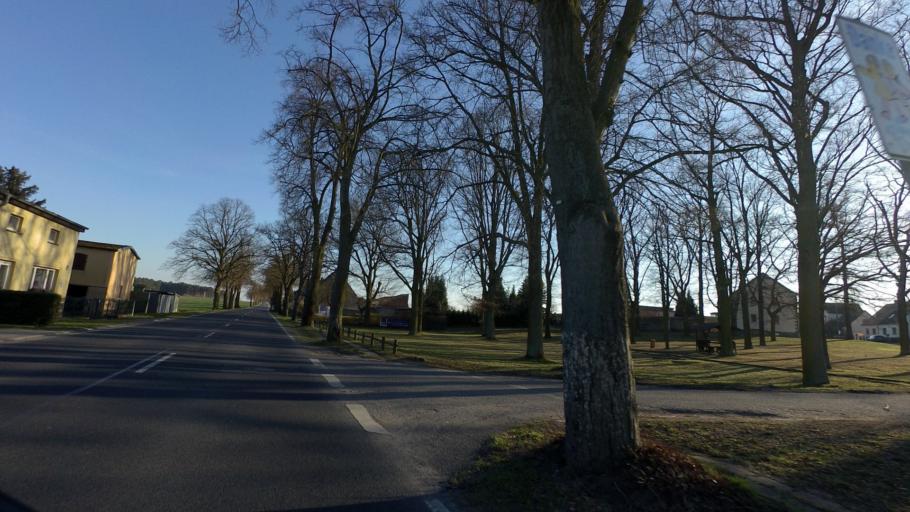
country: DE
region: Brandenburg
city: Britz
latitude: 52.9081
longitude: 13.8017
